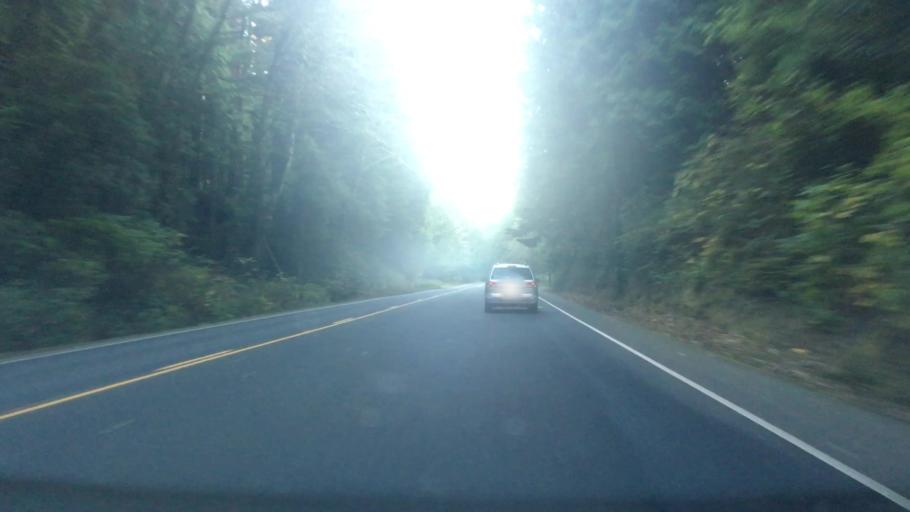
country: US
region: Oregon
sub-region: Clatsop County
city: Cannon Beach
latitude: 45.7864
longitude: -123.9587
